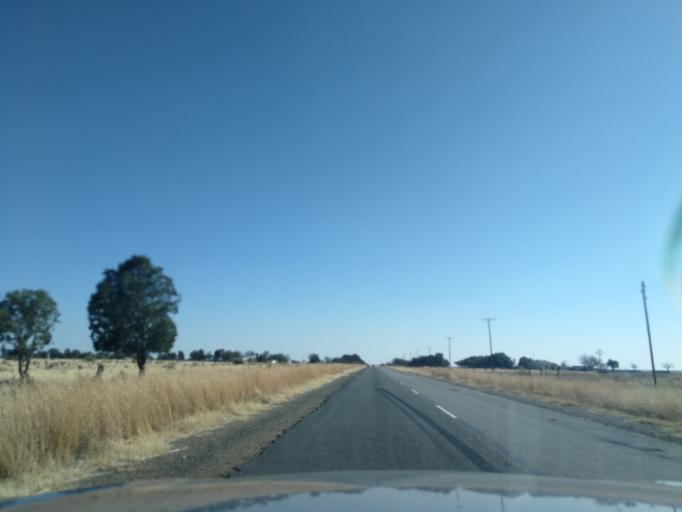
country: ZA
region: Orange Free State
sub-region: Fezile Dabi District Municipality
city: Kroonstad
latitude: -27.6138
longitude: 27.2010
